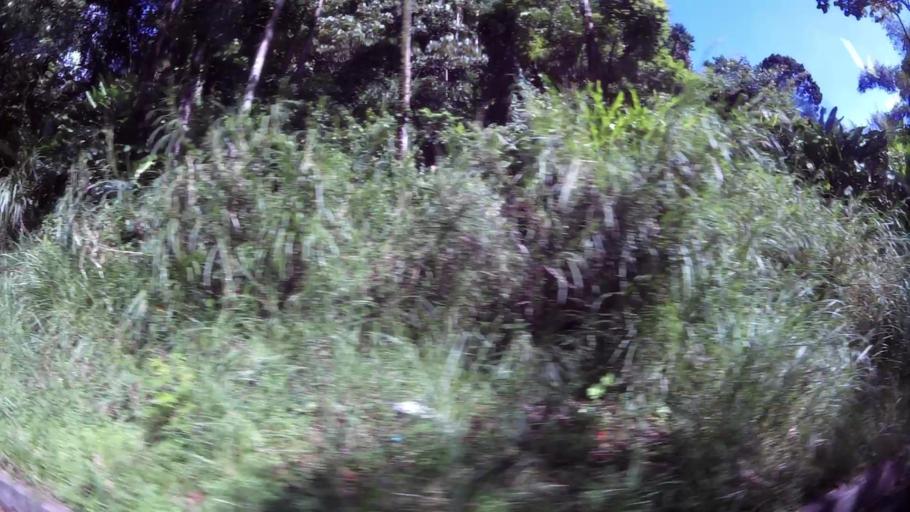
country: DM
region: Saint Paul
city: Pont Casse
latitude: 15.3468
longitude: -61.3663
